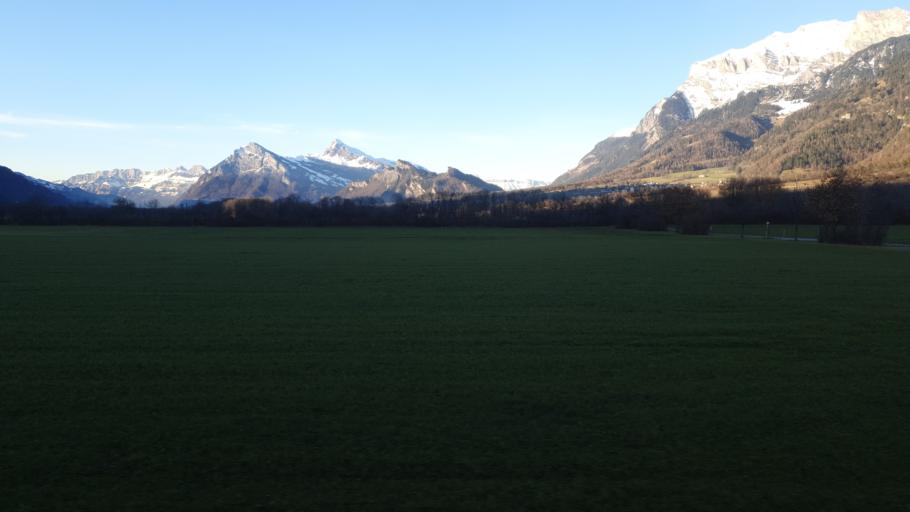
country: CH
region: Grisons
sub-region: Landquart District
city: Malans
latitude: 46.9750
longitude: 9.5647
